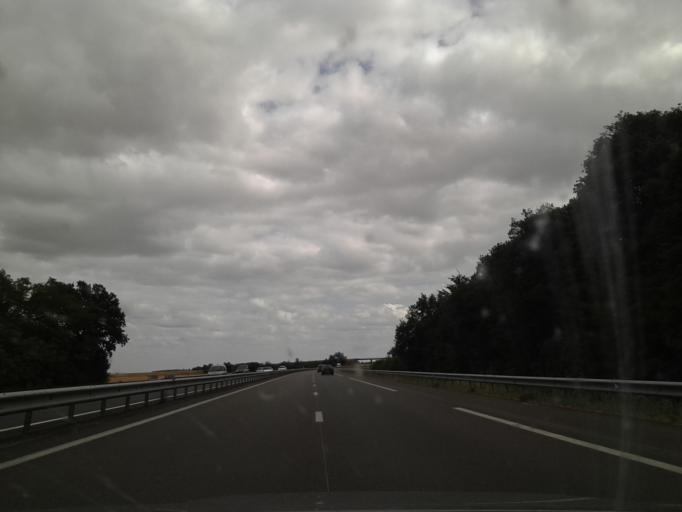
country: FR
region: Centre
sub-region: Departement du Cher
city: Levet
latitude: 46.9361
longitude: 2.4215
